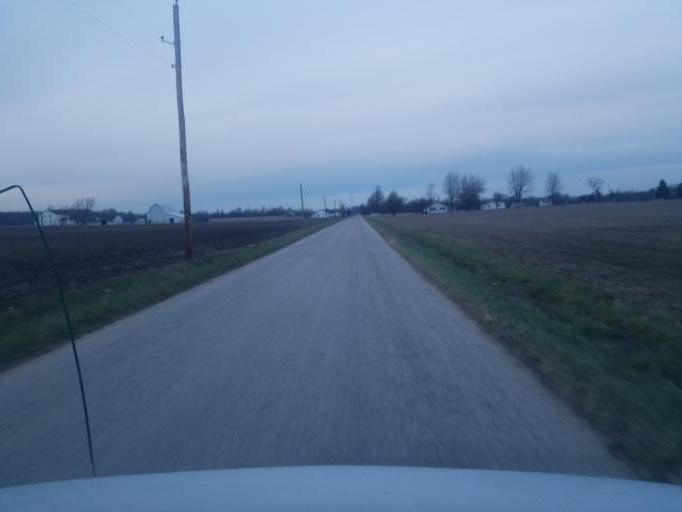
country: US
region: Indiana
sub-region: Adams County
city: Decatur
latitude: 40.7874
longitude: -84.8800
